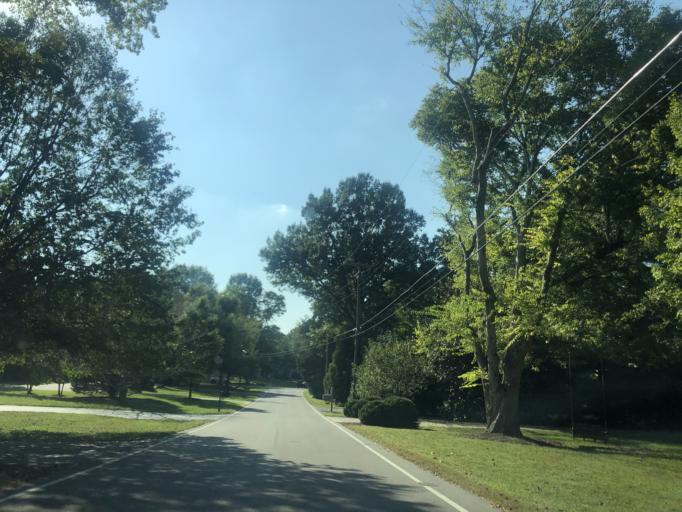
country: US
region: Tennessee
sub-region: Davidson County
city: Belle Meade
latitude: 36.1159
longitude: -86.8465
